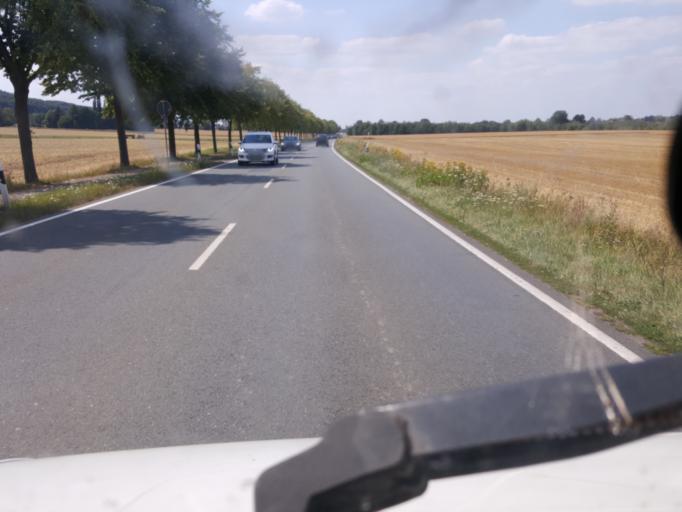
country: DE
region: North Rhine-Westphalia
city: Porta Westfalica
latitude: 52.2572
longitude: 8.8894
